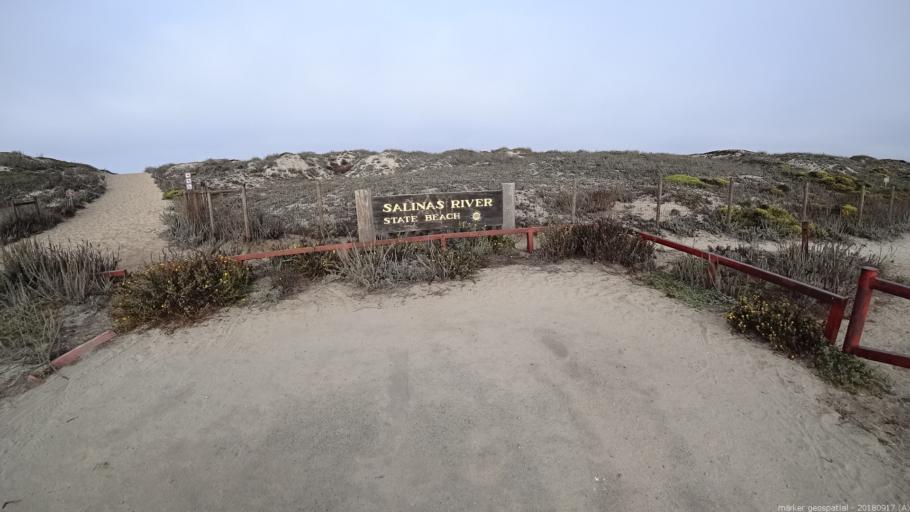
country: US
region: California
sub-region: Monterey County
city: Castroville
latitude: 36.7910
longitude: -121.7919
